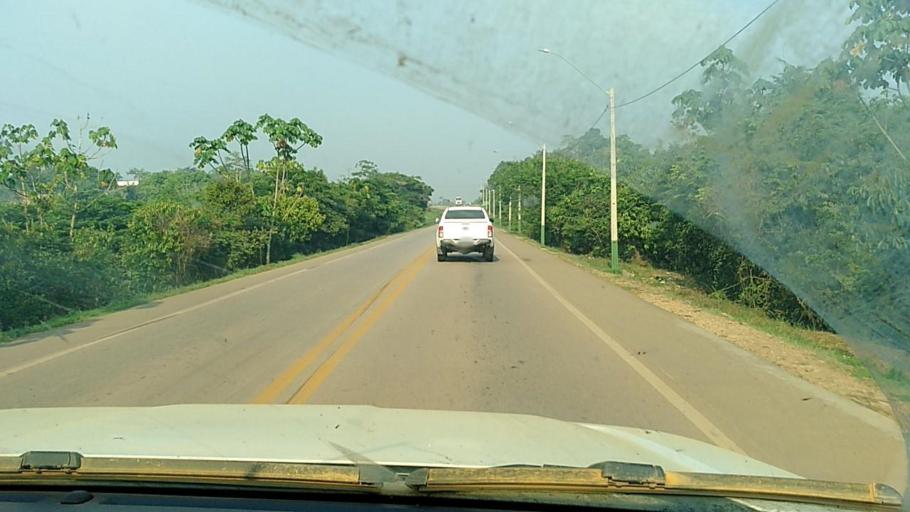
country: BR
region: Rondonia
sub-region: Porto Velho
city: Porto Velho
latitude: -8.7389
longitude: -63.9303
